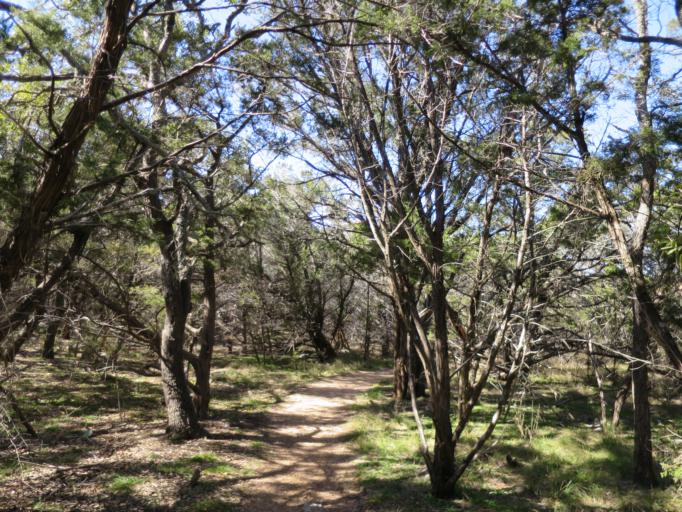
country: US
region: Texas
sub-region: Llano County
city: Kingsland
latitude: 30.6838
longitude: -98.3538
